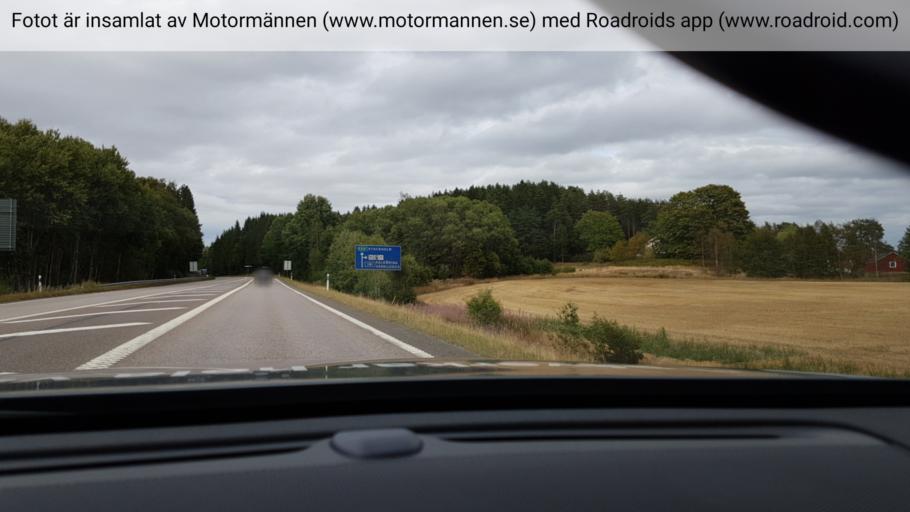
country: SE
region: Vaestra Goetaland
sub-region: Vargarda Kommun
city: Vargarda
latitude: 58.0455
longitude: 12.8068
